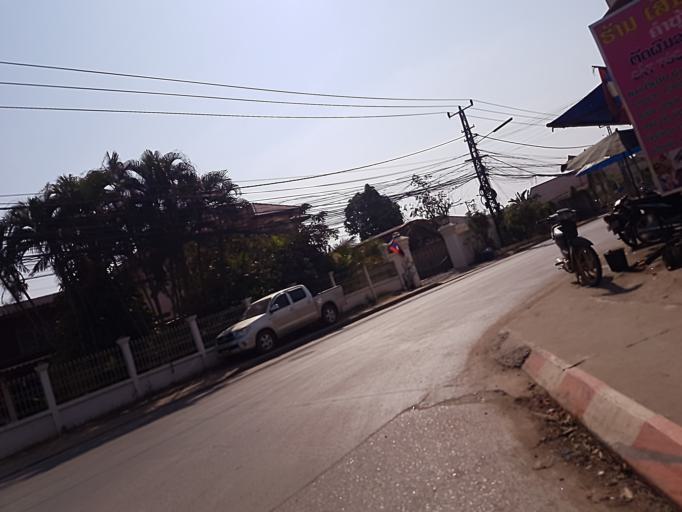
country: LA
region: Vientiane
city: Vientiane
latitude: 17.9449
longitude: 102.6383
